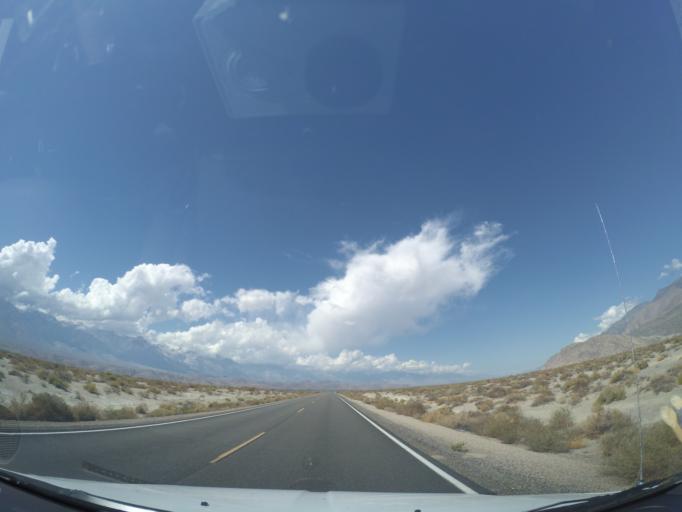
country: US
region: California
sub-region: Inyo County
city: Lone Pine
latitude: 36.5683
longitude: -117.9841
